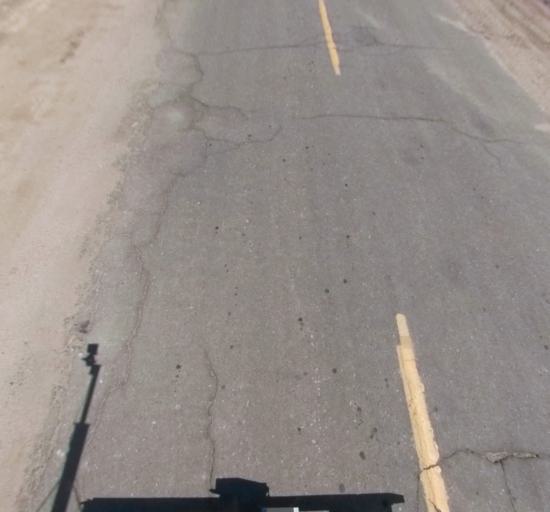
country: US
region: California
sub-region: Madera County
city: Chowchilla
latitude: 37.0412
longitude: -120.4013
